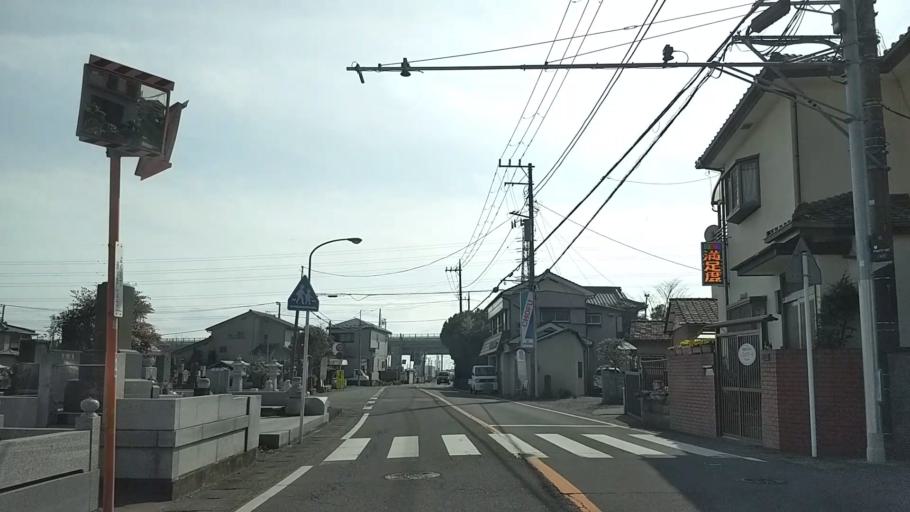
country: JP
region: Kanagawa
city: Chigasaki
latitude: 35.3536
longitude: 139.3847
